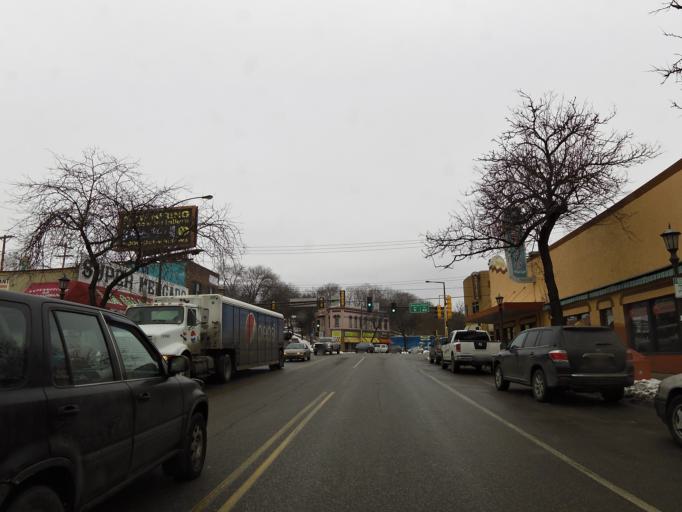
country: US
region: Minnesota
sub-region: Ramsey County
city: Saint Paul
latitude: 44.9296
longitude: -93.0773
